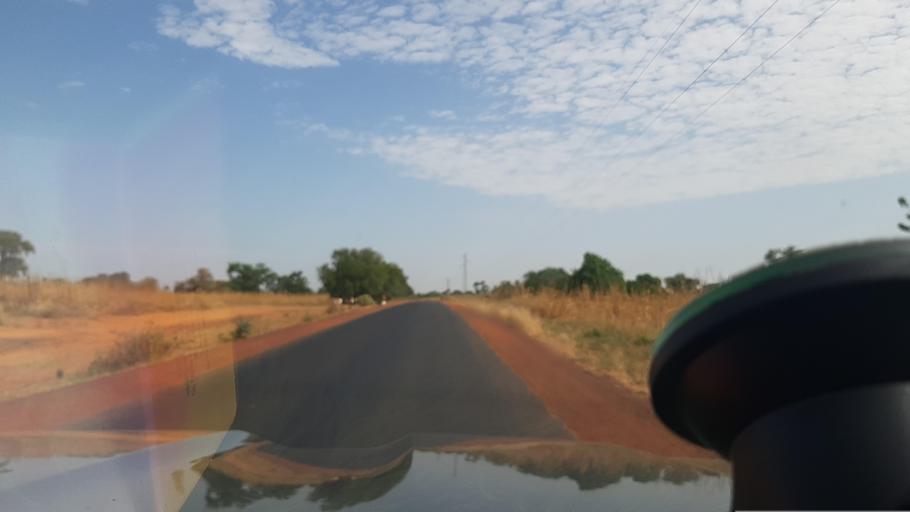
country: ML
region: Segou
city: Markala
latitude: 13.5666
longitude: -6.1089
